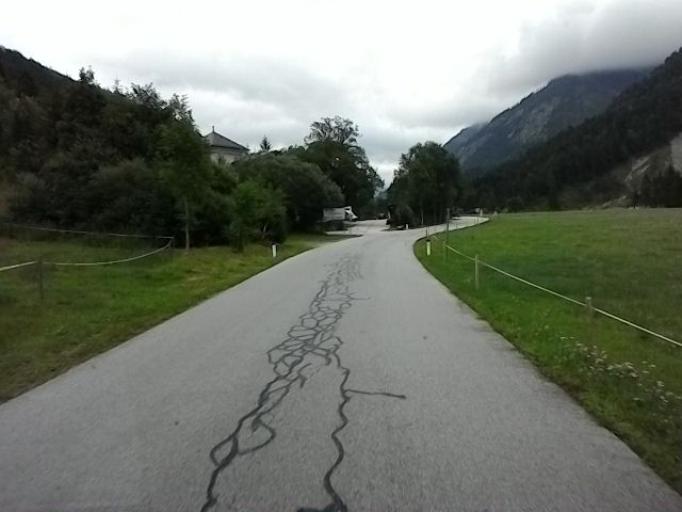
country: DE
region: Bavaria
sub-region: Upper Bavaria
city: Jachenau
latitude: 47.4676
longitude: 11.4838
